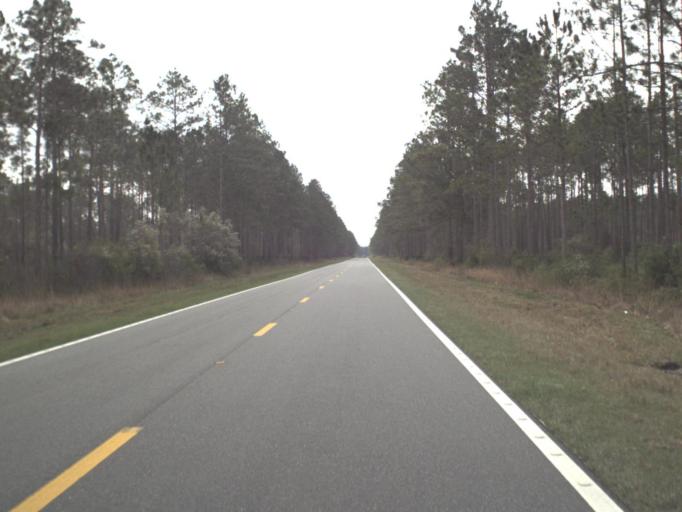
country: US
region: Florida
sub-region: Gulf County
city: Wewahitchka
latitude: 30.1033
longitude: -84.9860
